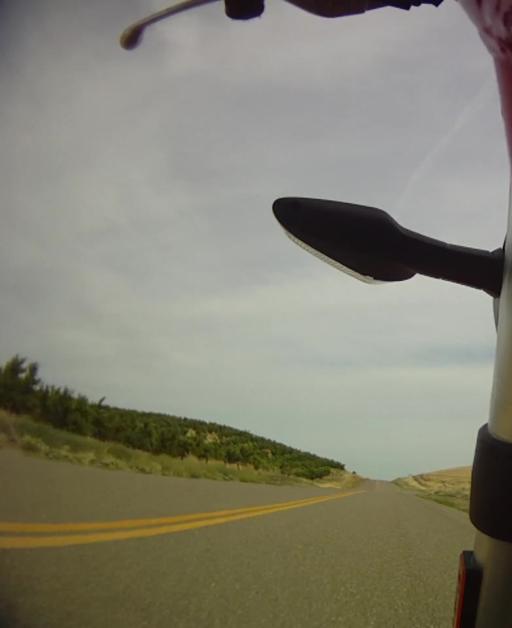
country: US
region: California
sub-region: Stanislaus County
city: Patterson
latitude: 37.4760
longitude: -121.2056
